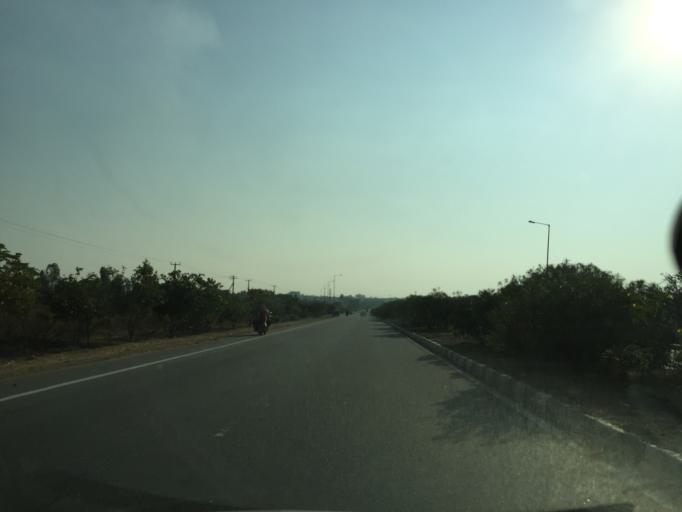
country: IN
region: Telangana
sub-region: Nalgonda
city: Bhongir
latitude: 17.5078
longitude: 78.8979
